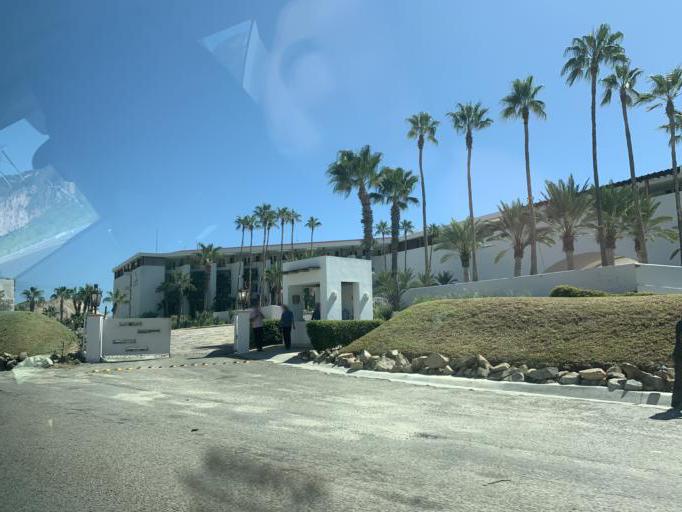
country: MX
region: Baja California Sur
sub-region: Los Cabos
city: San Jose del Cabo
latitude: 22.9865
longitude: -109.7585
